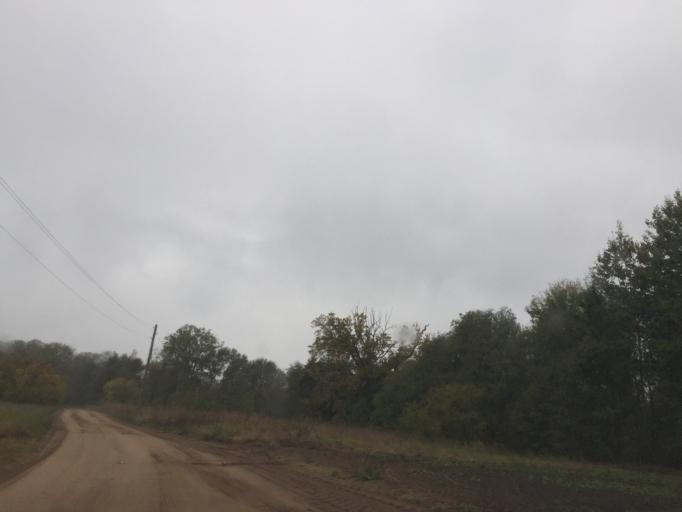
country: LV
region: Dobeles Rajons
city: Dobele
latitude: 56.6708
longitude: 23.4328
